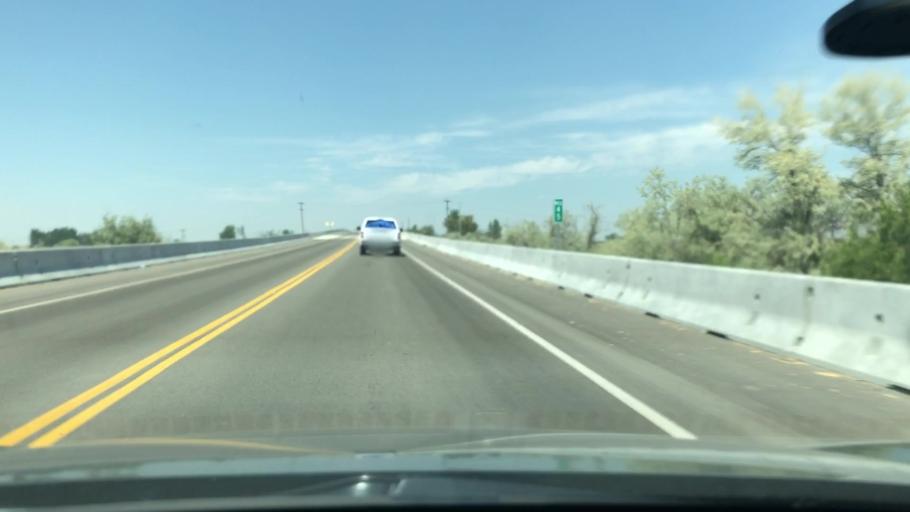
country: US
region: Idaho
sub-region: Canyon County
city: Parma
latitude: 43.7631
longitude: -116.9117
